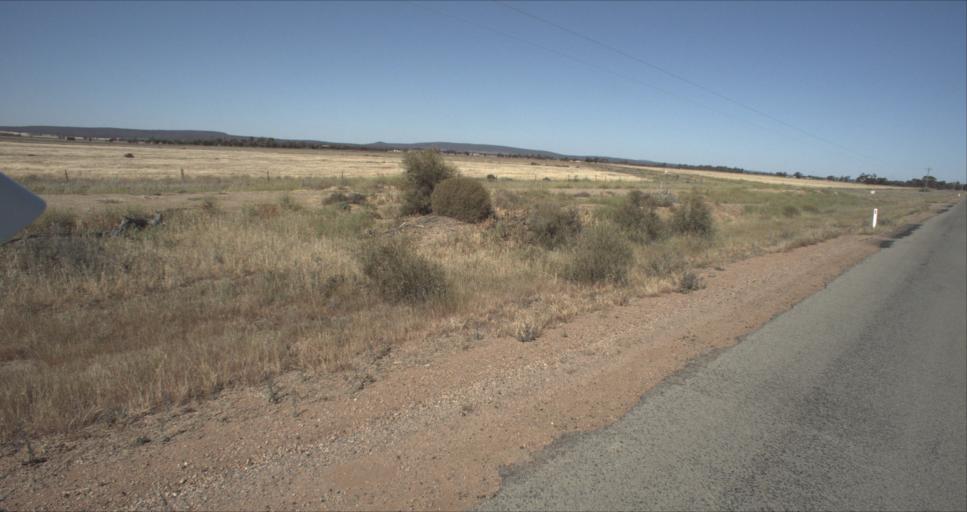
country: AU
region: New South Wales
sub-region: Leeton
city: Leeton
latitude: -34.4921
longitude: 146.3846
